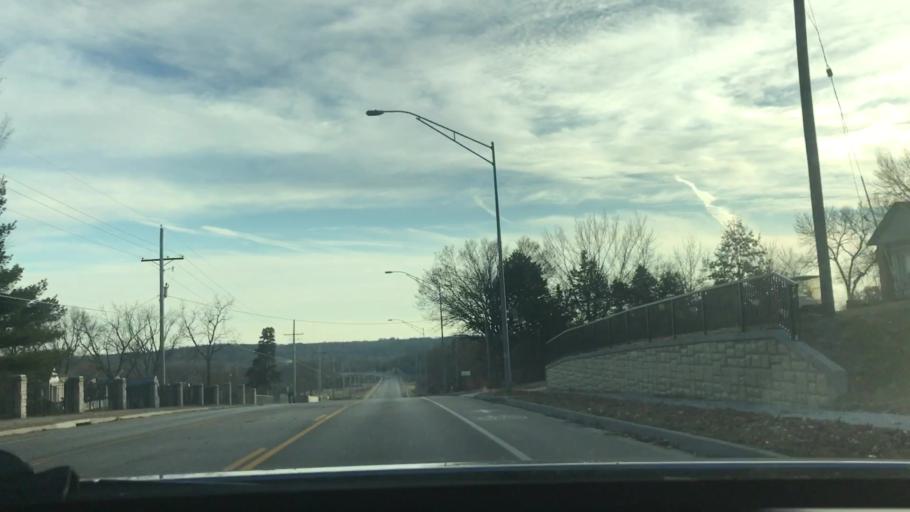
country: US
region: Missouri
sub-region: Jackson County
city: Independence
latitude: 39.0284
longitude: -94.3882
